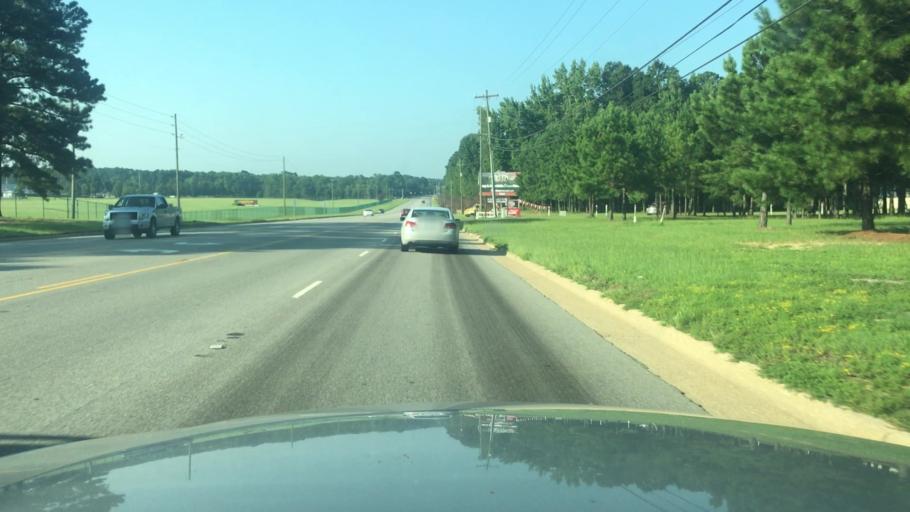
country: US
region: North Carolina
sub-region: Cumberland County
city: Eastover
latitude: 35.1753
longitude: -78.8590
